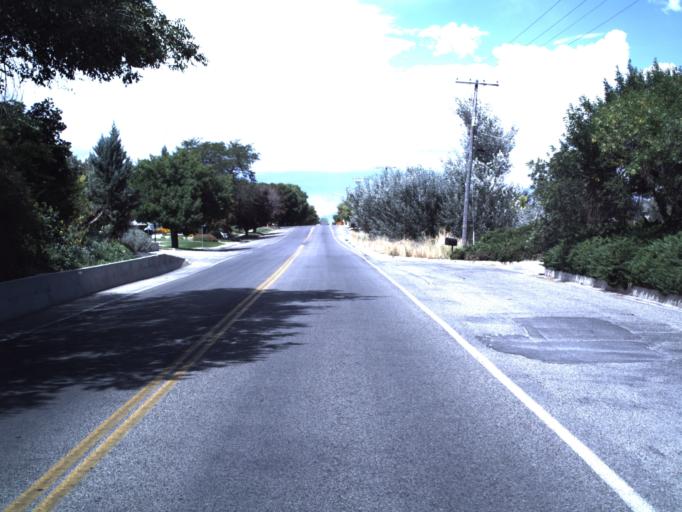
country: US
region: Utah
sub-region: Box Elder County
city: Tremonton
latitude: 41.7155
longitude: -112.1618
